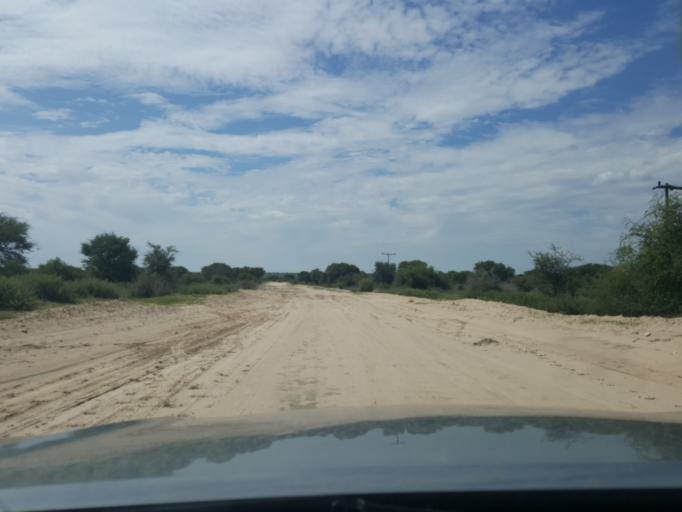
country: BW
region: Kweneng
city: Letlhakeng
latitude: -24.0674
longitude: 25.0303
